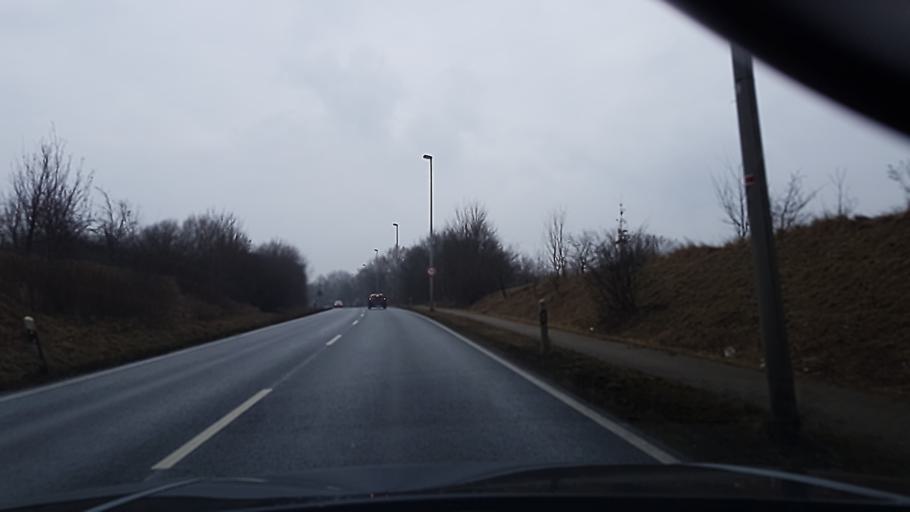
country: DE
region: Lower Saxony
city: Cramme
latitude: 52.1523
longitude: 10.4187
